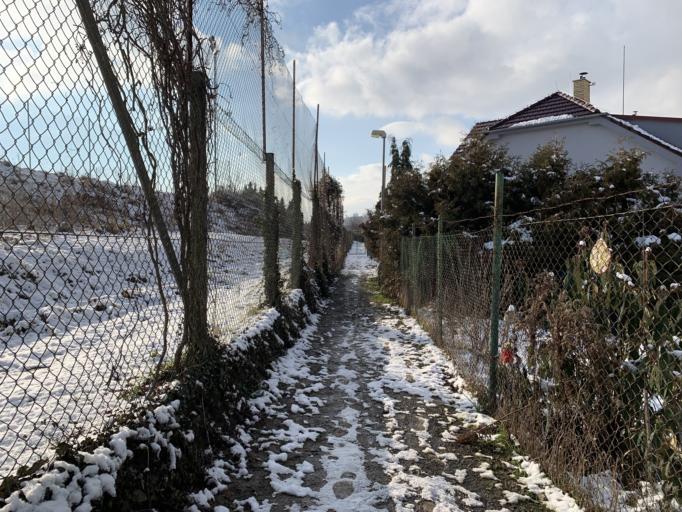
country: CZ
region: Praha
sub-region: Praha 8
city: Liben
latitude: 50.0667
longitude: 14.4860
